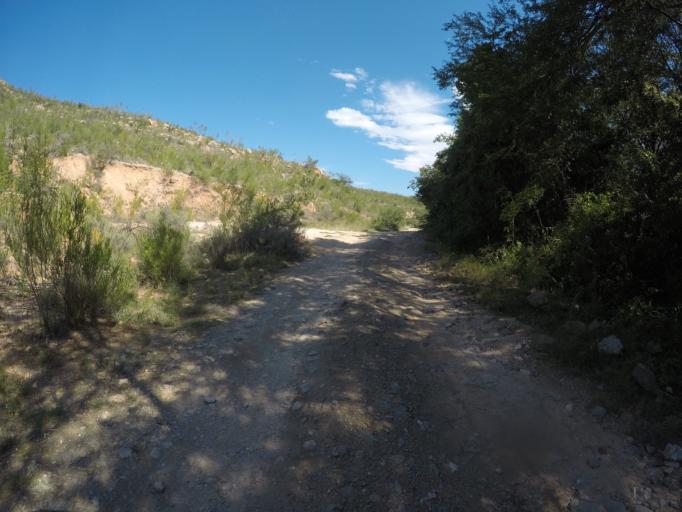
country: ZA
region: Eastern Cape
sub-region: Cacadu District Municipality
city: Kareedouw
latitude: -33.6464
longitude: 24.4635
